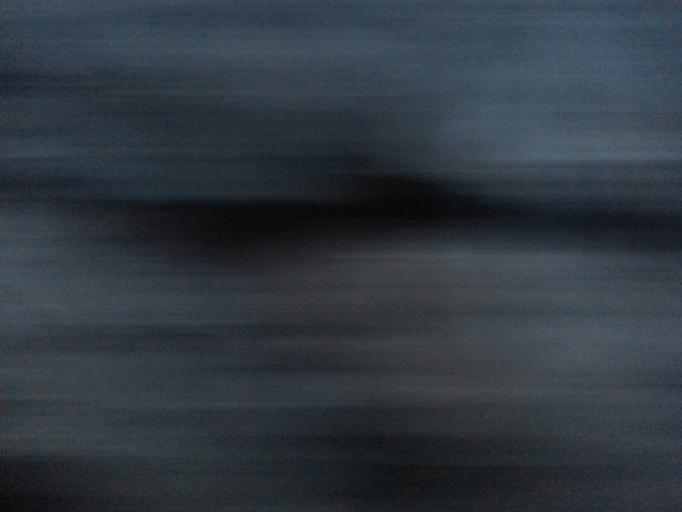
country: NO
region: Sor-Trondelag
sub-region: Rennebu
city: Berkak
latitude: 62.7734
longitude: 9.9887
